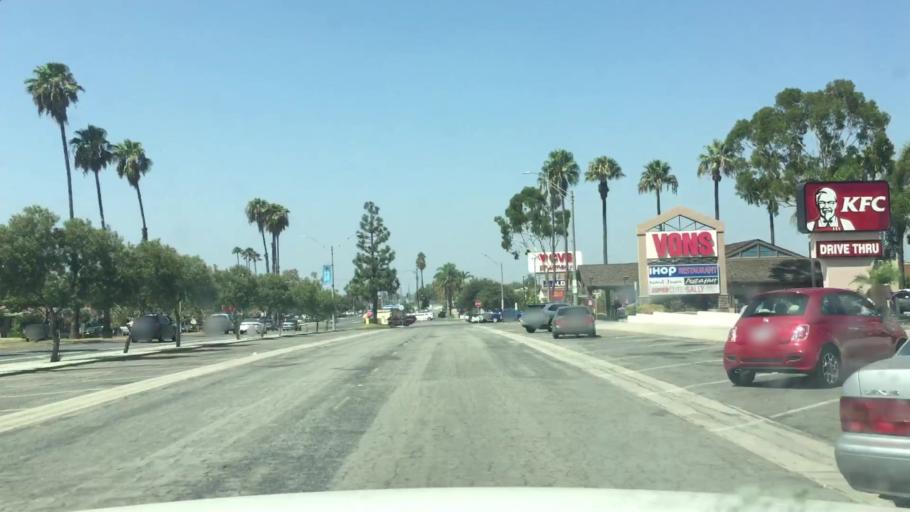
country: US
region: California
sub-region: Los Angeles County
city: Signal Hill
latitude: 33.8406
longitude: -118.1847
